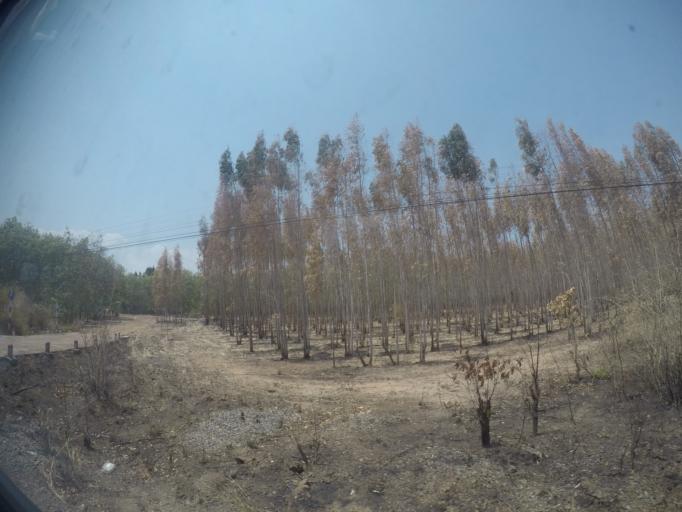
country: VN
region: Binh Thuan
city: Thuan Nam
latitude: 10.9283
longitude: 107.9108
